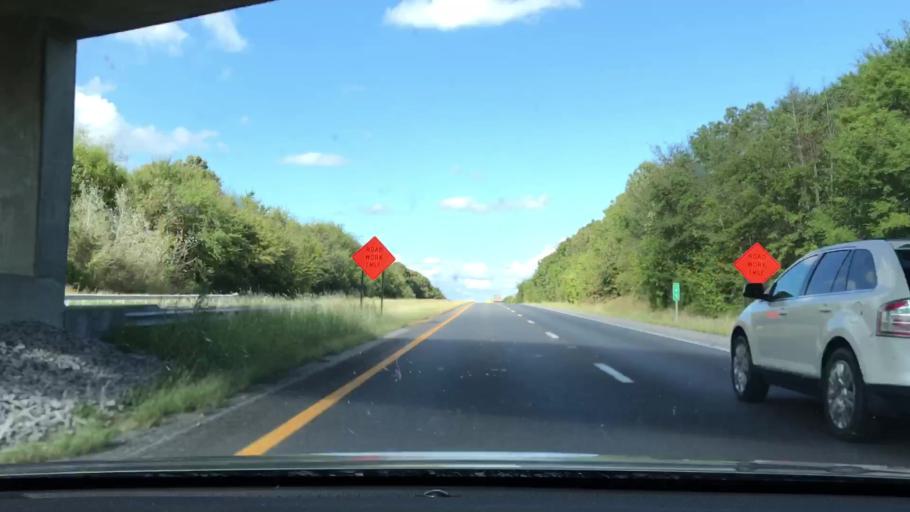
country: US
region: Kentucky
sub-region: Marshall County
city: Calvert City
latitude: 36.9558
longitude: -88.3494
